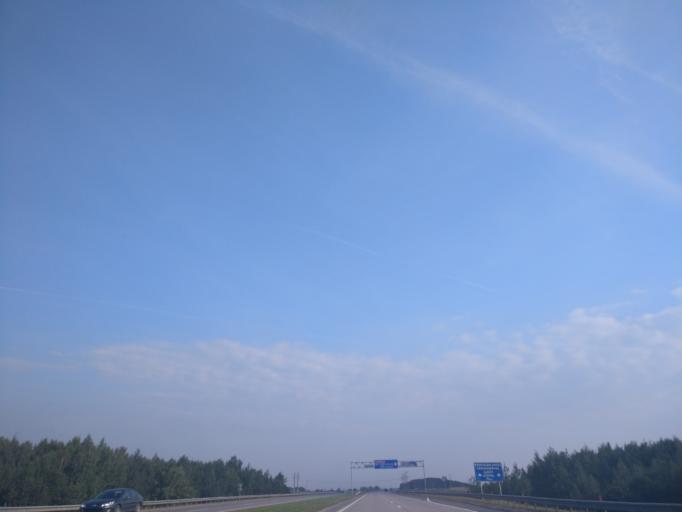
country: BY
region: Minsk
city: Astrashytski Haradok
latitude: 54.0489
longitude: 27.7020
